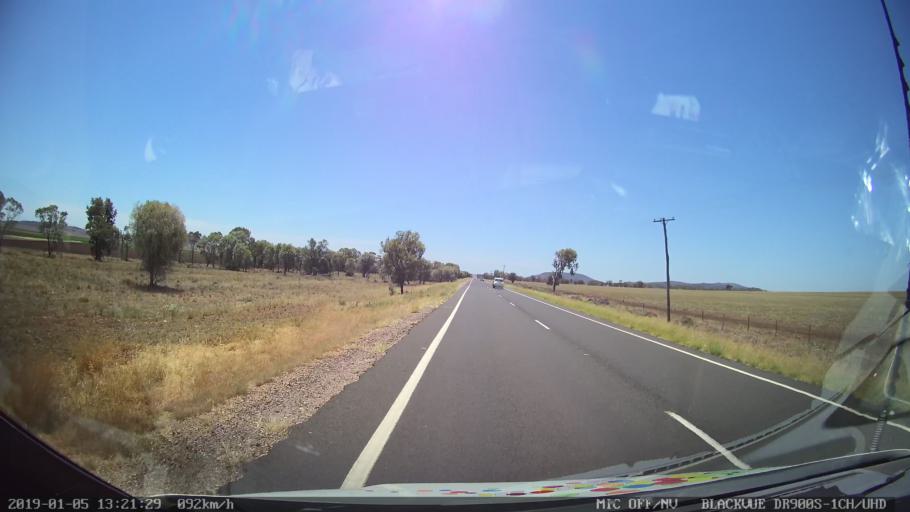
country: AU
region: New South Wales
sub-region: Gunnedah
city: Gunnedah
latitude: -31.0940
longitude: 149.9492
